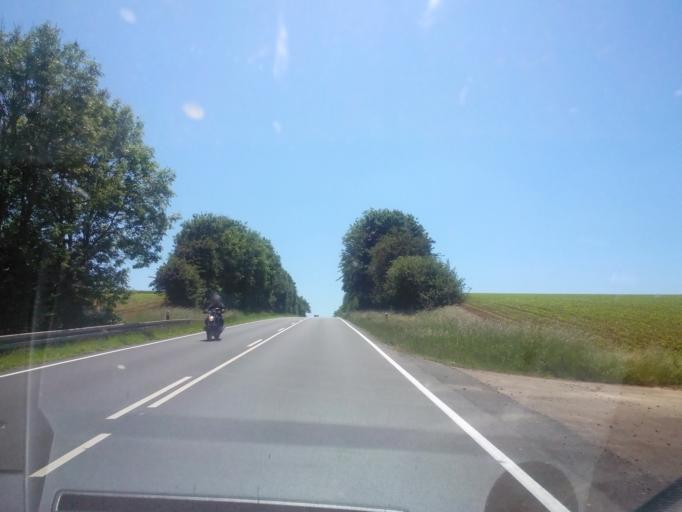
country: DE
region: Rheinland-Pfalz
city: Kirf
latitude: 49.5222
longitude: 6.4585
